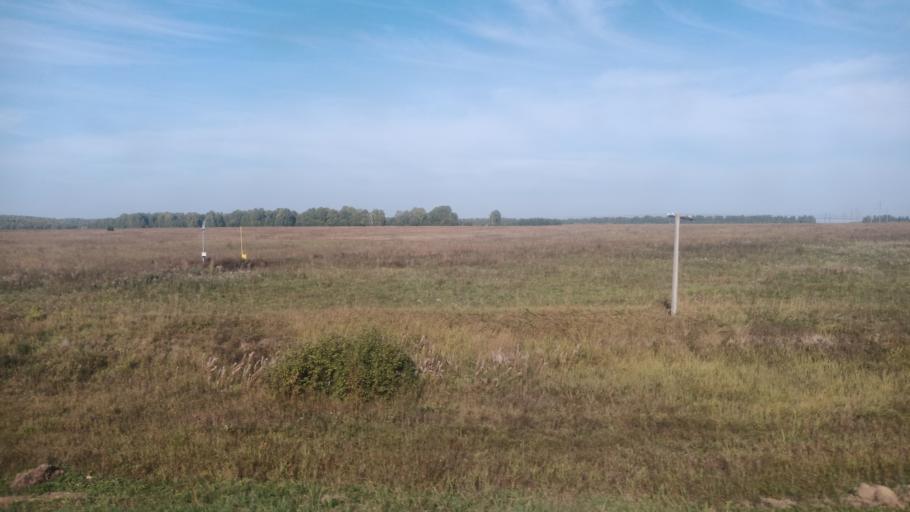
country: RU
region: Altai Krai
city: Troitskoye
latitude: 53.0984
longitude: 84.6743
